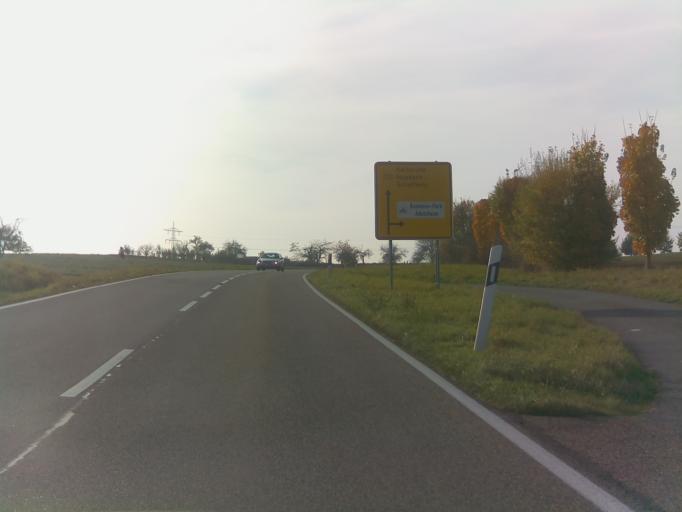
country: DE
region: Baden-Wuerttemberg
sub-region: Karlsruhe Region
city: Adelsheim
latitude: 49.4068
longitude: 9.3740
